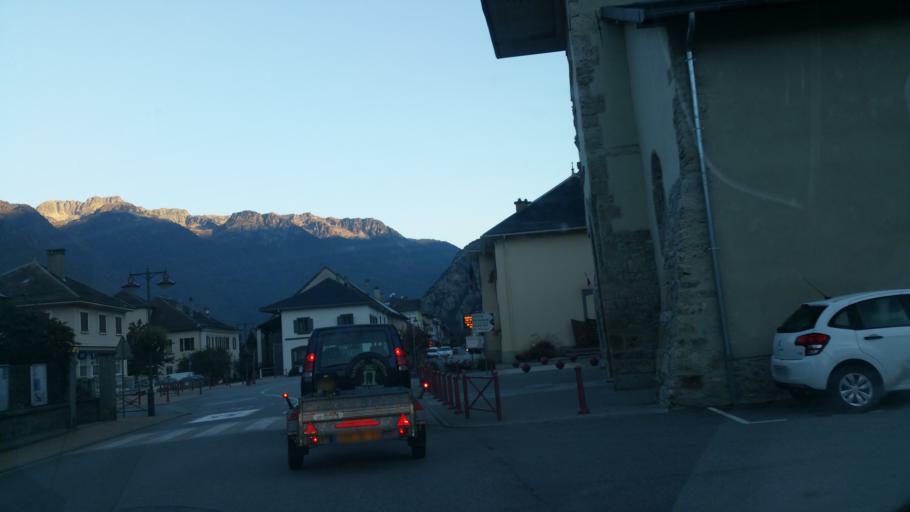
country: FR
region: Rhone-Alpes
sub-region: Departement de la Savoie
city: La Chambre
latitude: 45.3584
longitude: 6.3003
